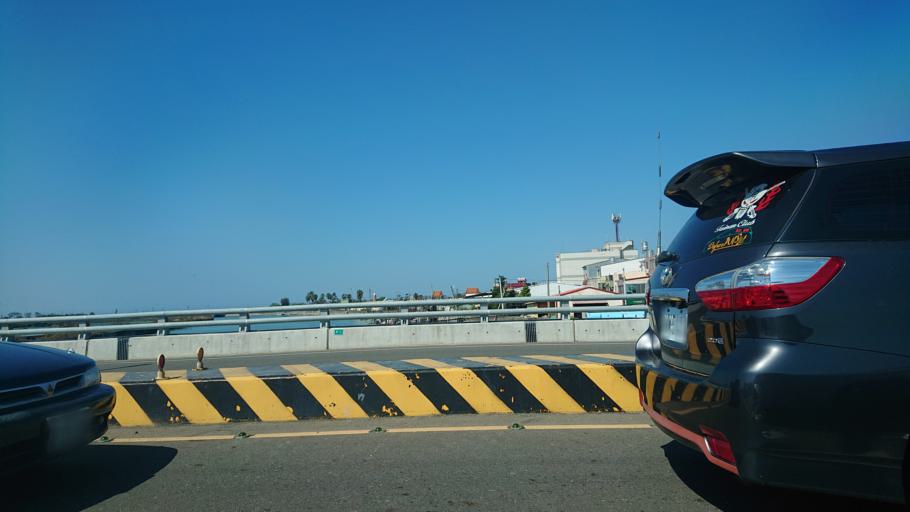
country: TW
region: Taiwan
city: Xinying
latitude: 23.2833
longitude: 120.1355
